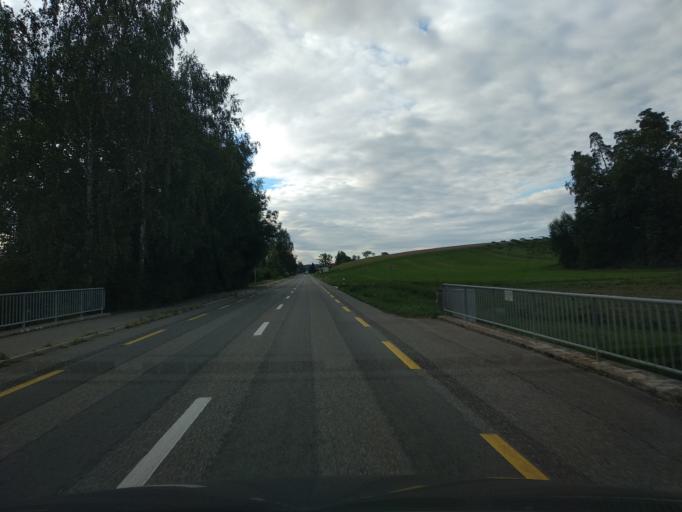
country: DE
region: Baden-Wuerttemberg
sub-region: Freiburg Region
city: Busingen
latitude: 47.6755
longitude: 8.6911
